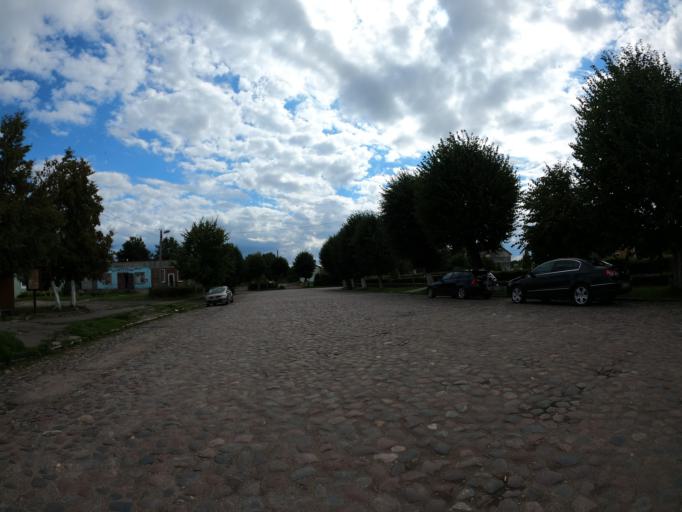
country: RU
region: Kaliningrad
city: Zheleznodorozhnyy
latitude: 54.3602
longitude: 21.3066
